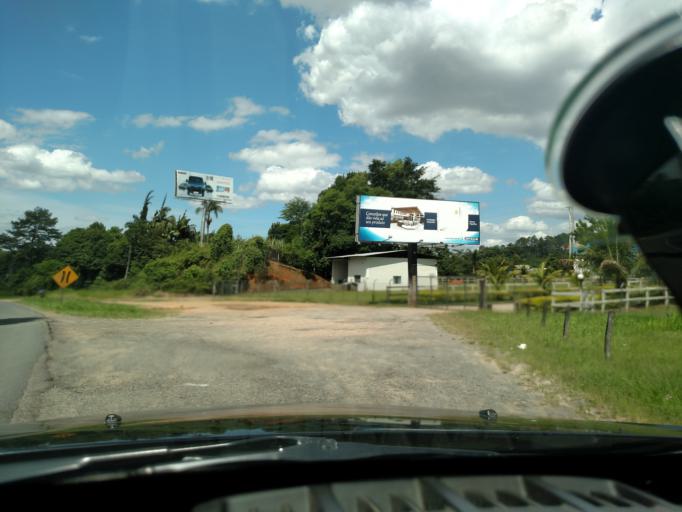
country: BR
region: Santa Catarina
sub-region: Blumenau
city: Blumenau
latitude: -26.8712
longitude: -49.1087
